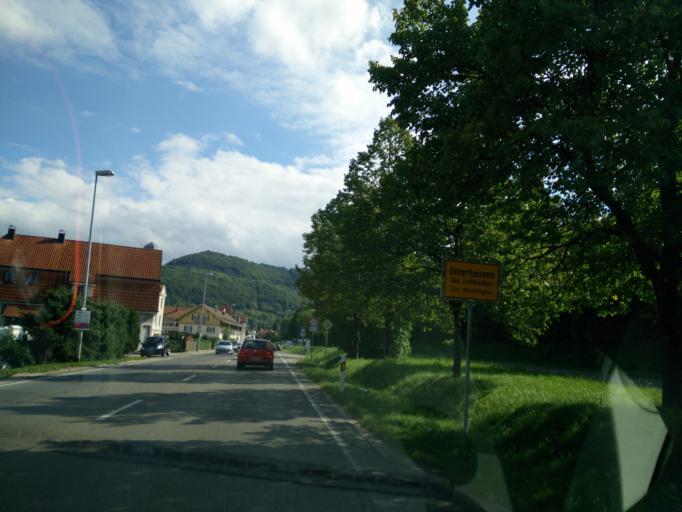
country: DE
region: Baden-Wuerttemberg
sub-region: Tuebingen Region
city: Pfullingen
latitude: 48.4433
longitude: 9.2470
